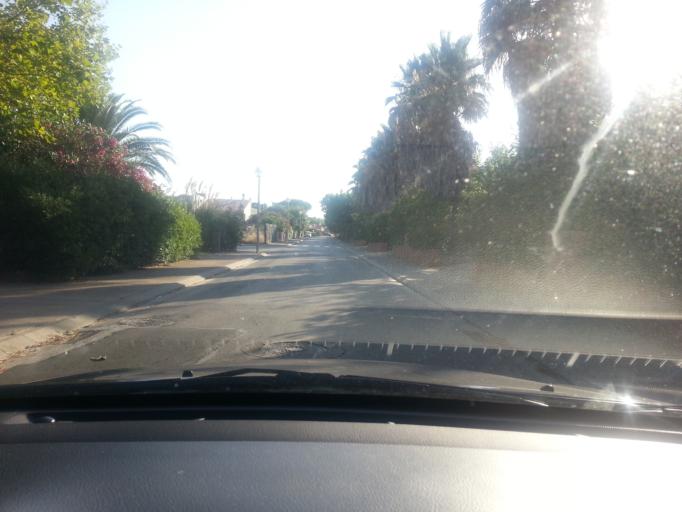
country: ES
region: Catalonia
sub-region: Provincia de Girona
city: Pals
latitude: 42.0106
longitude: 3.1923
